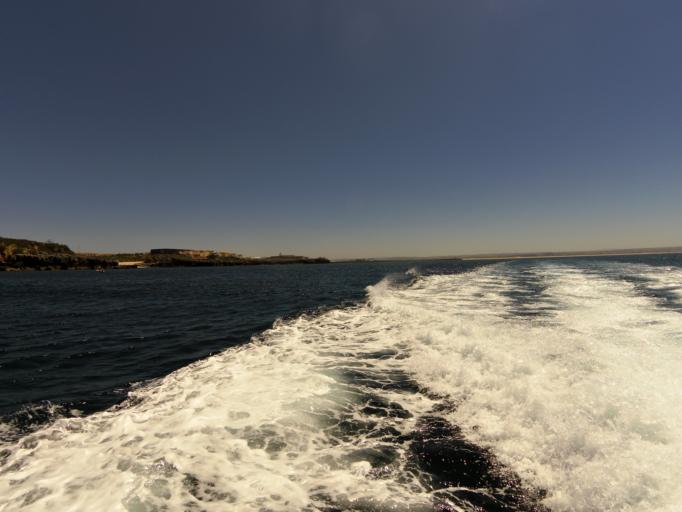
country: PT
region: Leiria
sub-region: Peniche
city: Peniche
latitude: 39.3511
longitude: -9.3926
